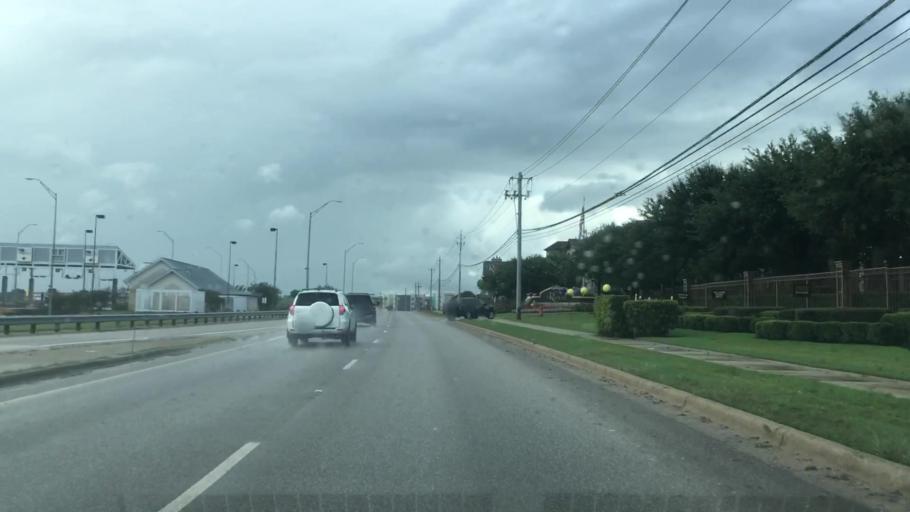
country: US
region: Texas
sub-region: Williamson County
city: Jollyville
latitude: 30.4757
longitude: -97.7736
